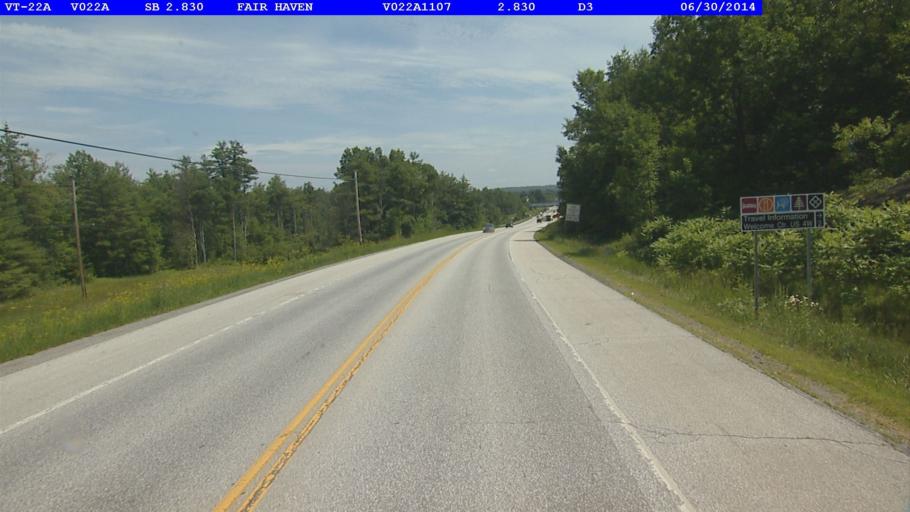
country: US
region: Vermont
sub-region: Rutland County
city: Fair Haven
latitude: 43.6096
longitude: -73.2822
